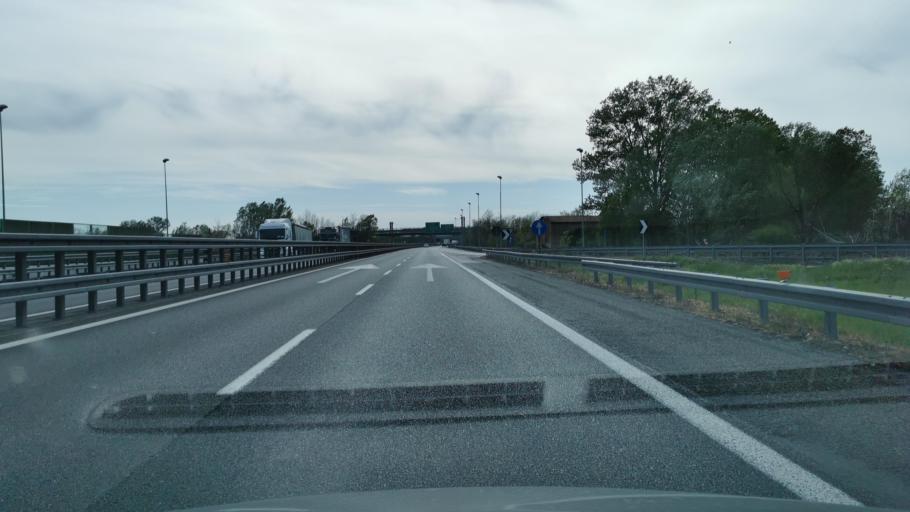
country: IT
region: Piedmont
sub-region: Provincia di Alessandria
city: Alessandria
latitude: 44.9383
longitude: 8.5787
